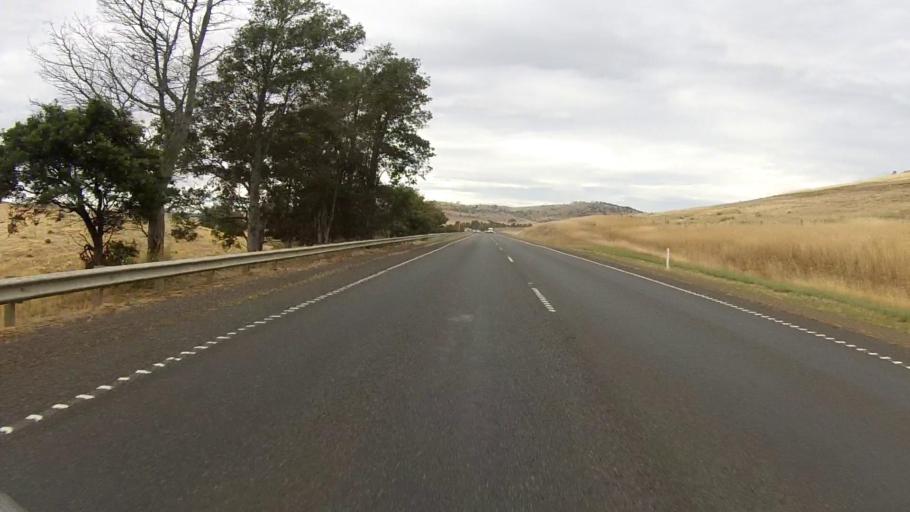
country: AU
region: Tasmania
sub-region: Brighton
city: Bridgewater
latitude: -42.3766
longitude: 147.3261
